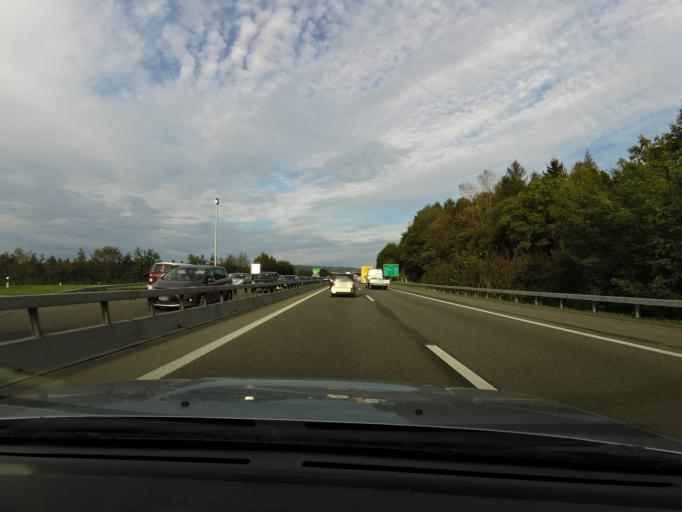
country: CH
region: Aargau
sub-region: Bezirk Lenzburg
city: Othmarsingen
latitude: 47.4202
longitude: 8.2260
